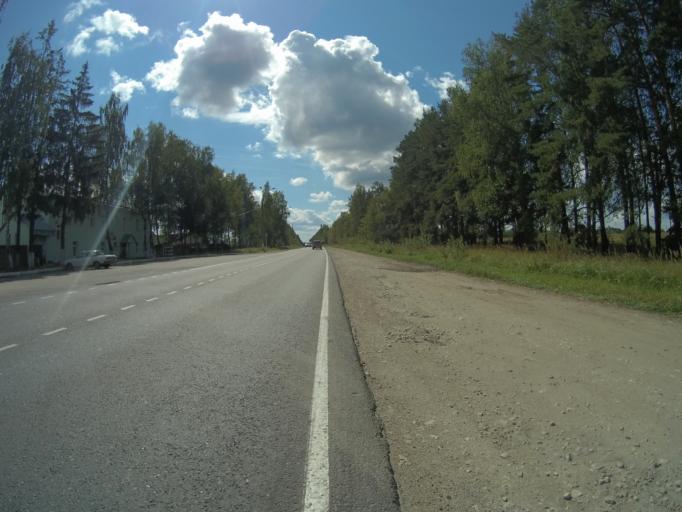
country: RU
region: Vladimir
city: Golovino
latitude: 55.9992
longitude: 40.5641
